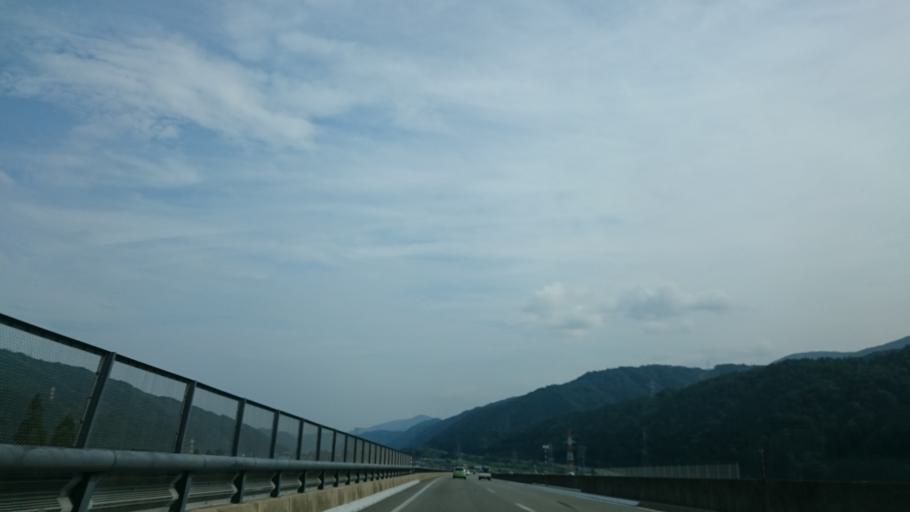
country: JP
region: Gifu
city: Gujo
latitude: 35.8558
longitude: 136.8714
